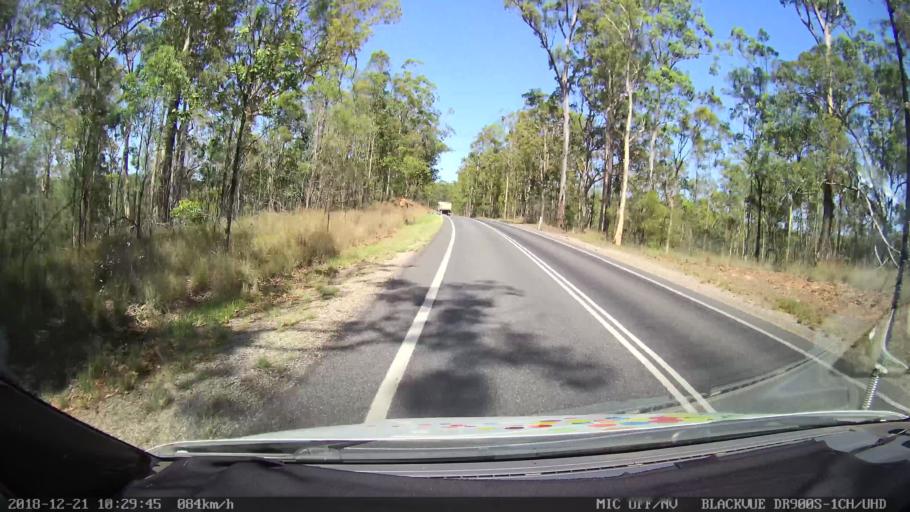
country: AU
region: New South Wales
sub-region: Clarence Valley
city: South Grafton
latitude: -29.6322
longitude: 152.7175
